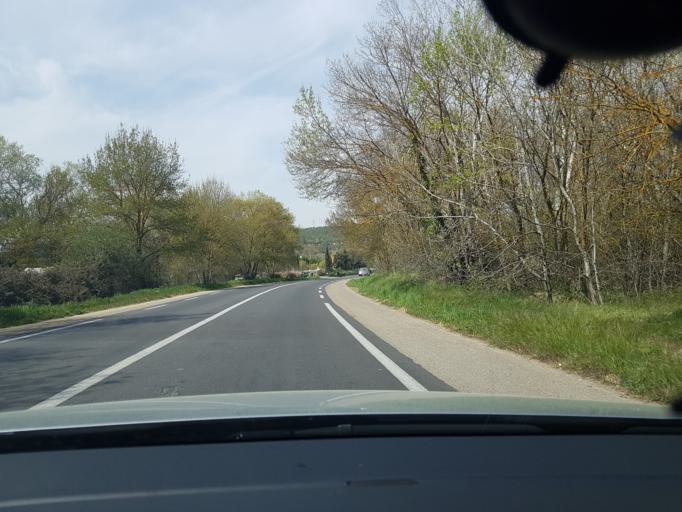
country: FR
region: Provence-Alpes-Cote d'Azur
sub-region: Departement des Bouches-du-Rhone
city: Gardanne
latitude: 43.4667
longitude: 5.4618
